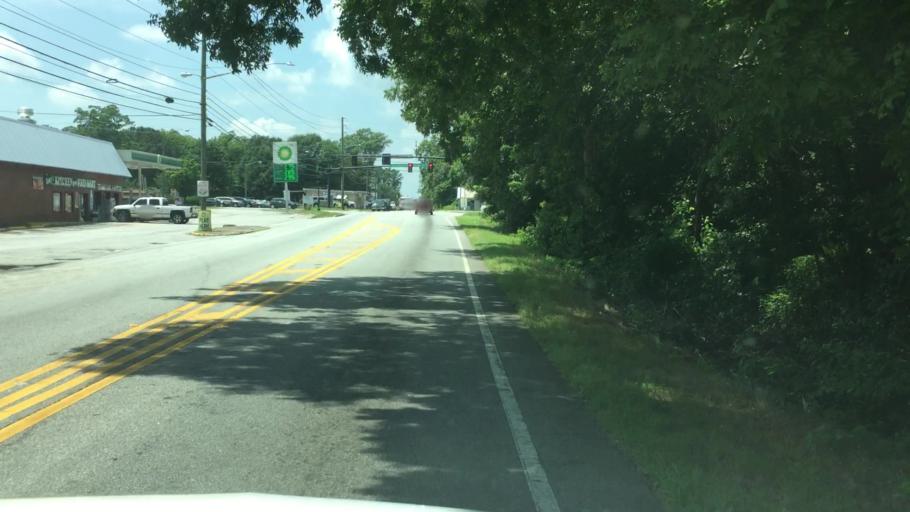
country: US
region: Georgia
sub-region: Barrow County
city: Auburn
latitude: 34.0048
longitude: -83.8105
